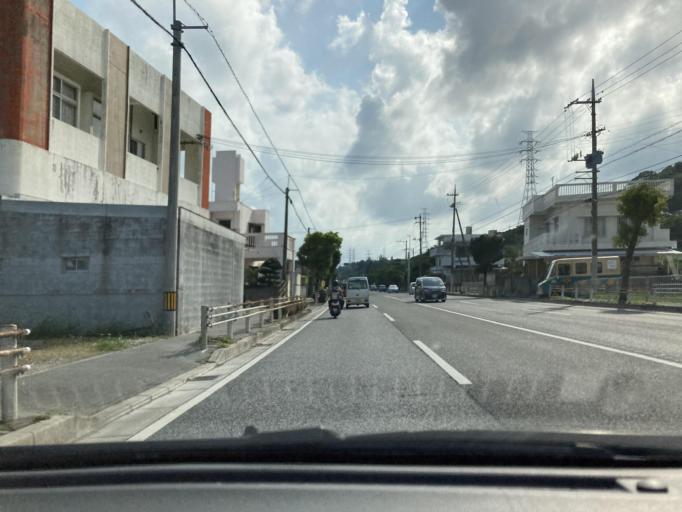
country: JP
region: Okinawa
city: Ginowan
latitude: 26.2609
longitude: 127.7876
